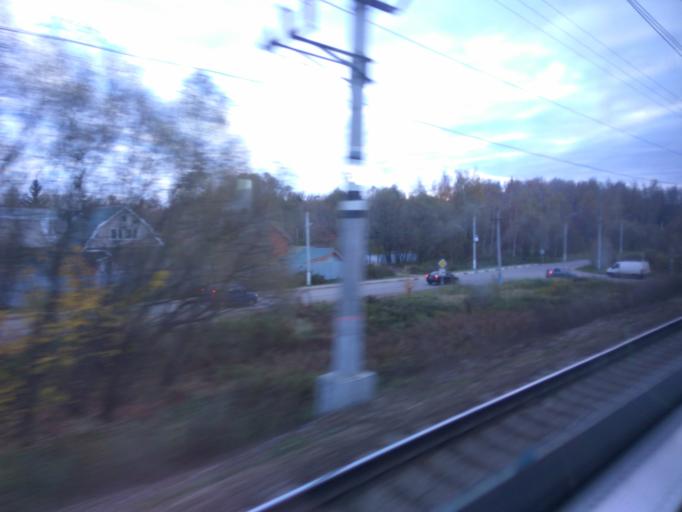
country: RU
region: Moskovskaya
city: Aprelevka
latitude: 55.5459
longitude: 37.0564
